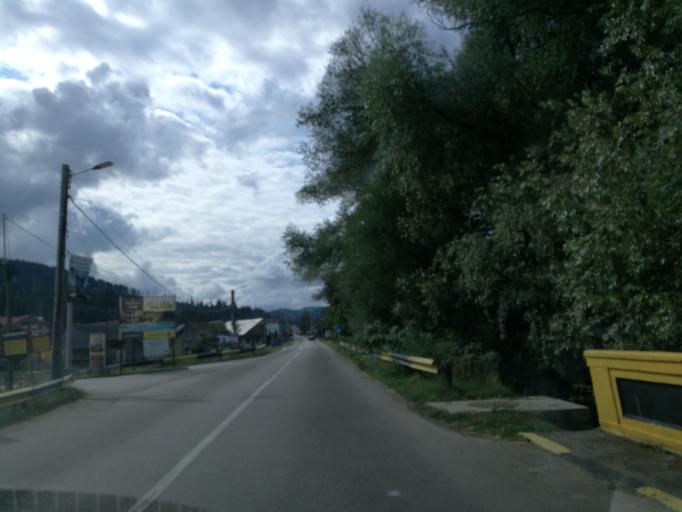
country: RO
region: Suceava
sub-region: Oras Gura Humorului
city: Gura Humorului
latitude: 47.5386
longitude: 25.8643
